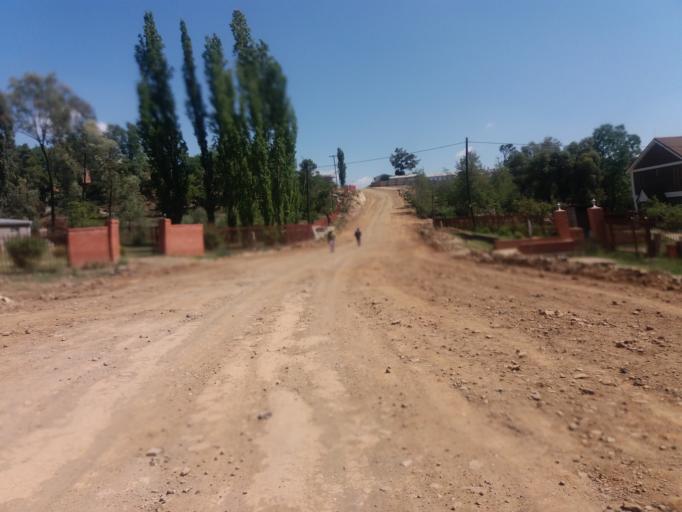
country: LS
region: Maseru
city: Maseru
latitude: -29.3192
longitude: 27.5042
